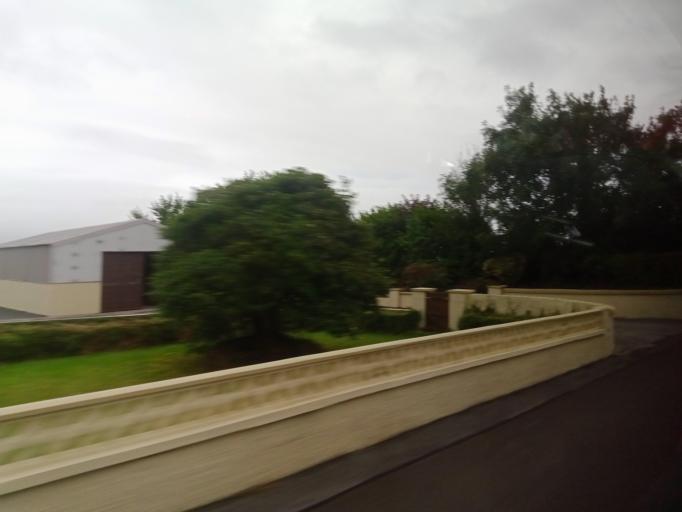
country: IE
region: Munster
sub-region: Waterford
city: Dungarvan
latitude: 52.0478
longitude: -7.6006
